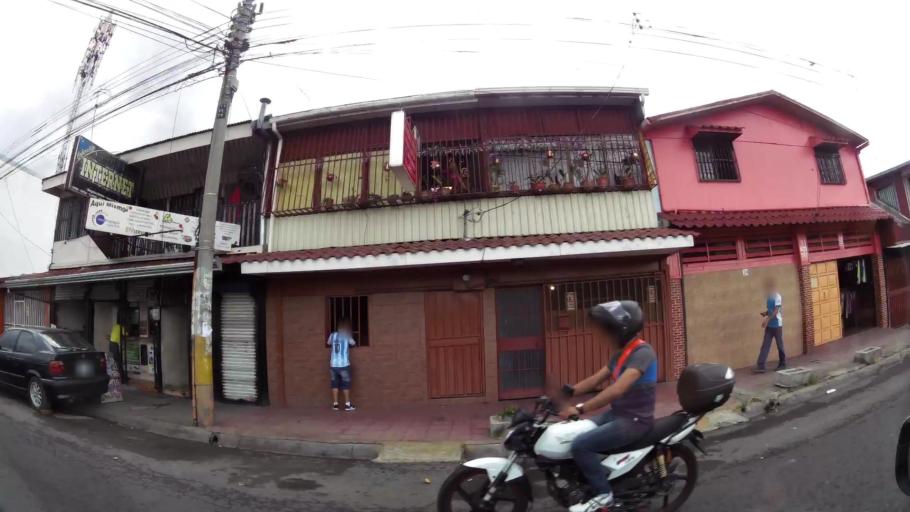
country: CR
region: San Jose
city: San Rafael
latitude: 9.9217
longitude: -84.1188
